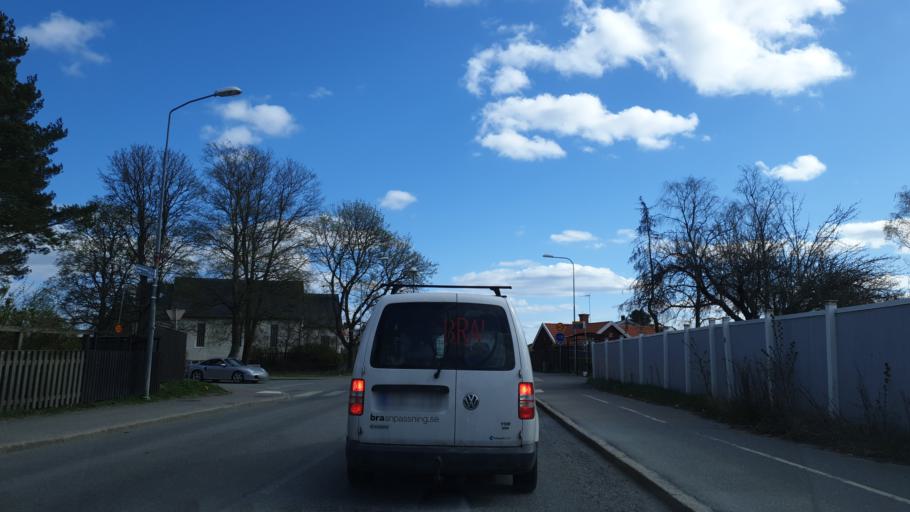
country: SE
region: Uppsala
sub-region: Uppsala Kommun
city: Gamla Uppsala
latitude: 59.8951
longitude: 17.6368
